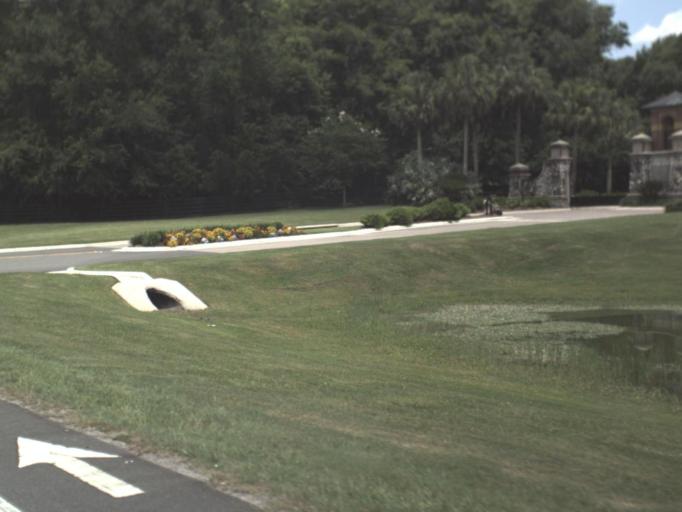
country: US
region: Florida
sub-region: Alachua County
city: Gainesville
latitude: 29.5947
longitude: -82.3832
